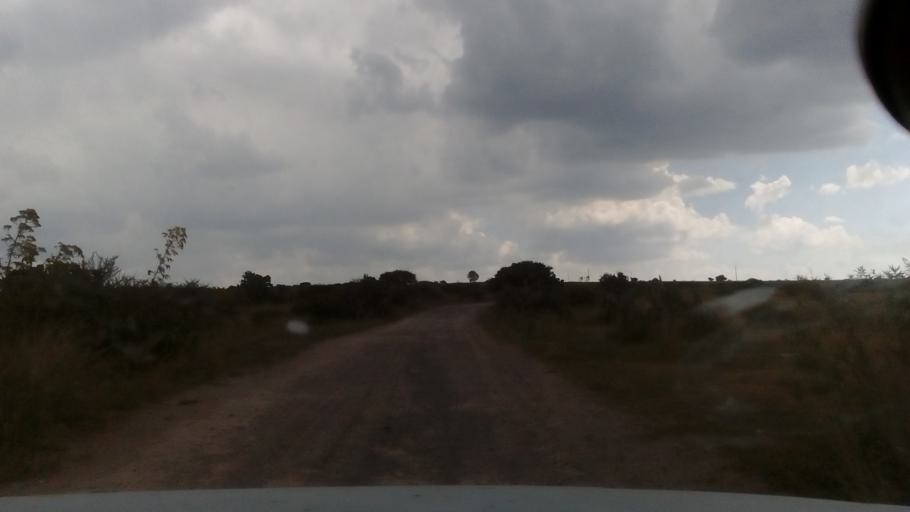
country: MX
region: Guanajuato
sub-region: Silao de la Victoria
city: San Francisco (Banos de Agua Caliente)
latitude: 21.1896
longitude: -101.4191
